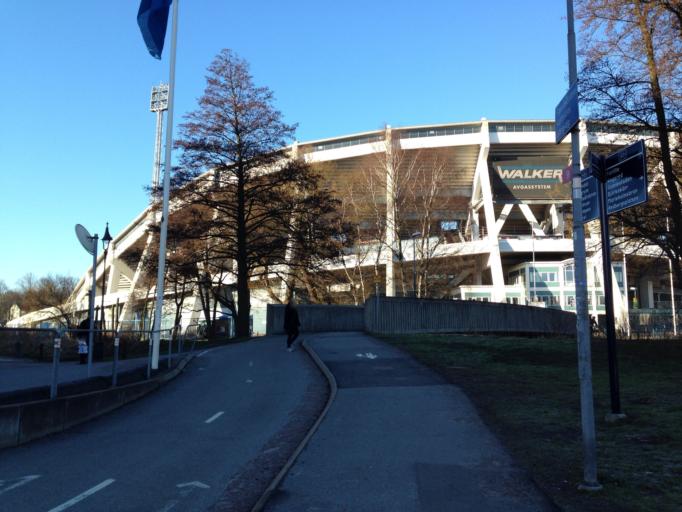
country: SE
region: Vaestra Goetaland
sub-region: Goteborg
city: Goeteborg
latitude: 57.7070
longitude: 11.9901
